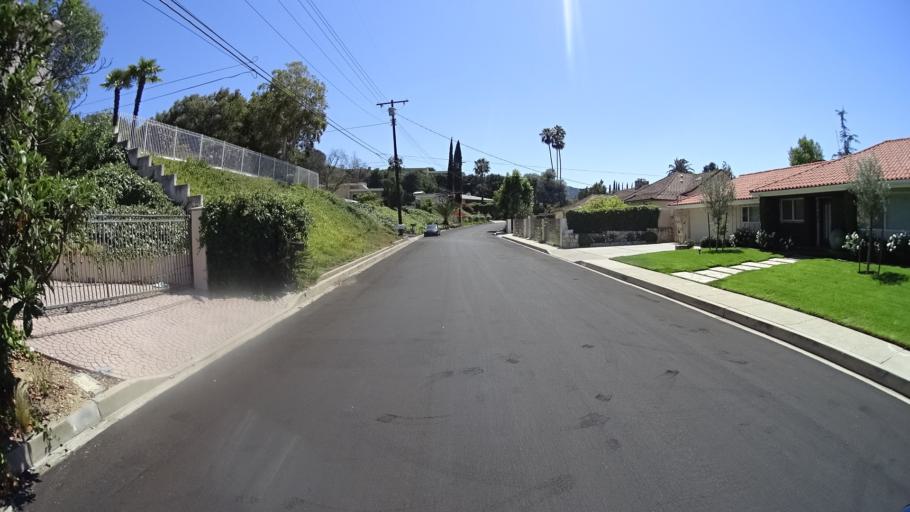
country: US
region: California
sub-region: Los Angeles County
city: Sherman Oaks
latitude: 34.1407
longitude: -118.4880
